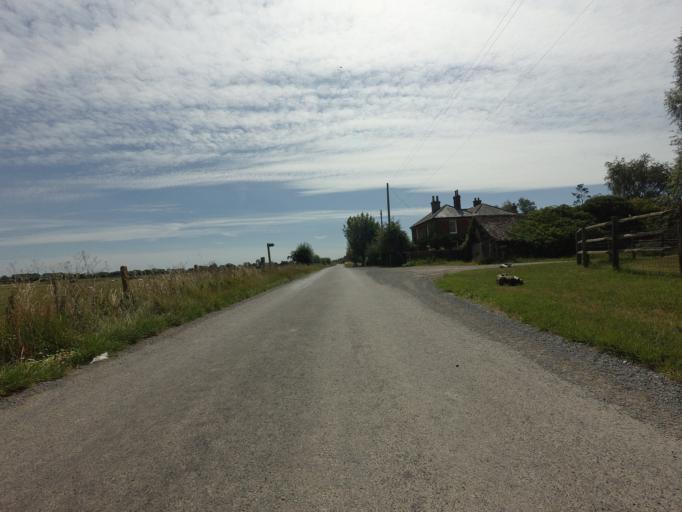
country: GB
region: England
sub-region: Kent
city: Stone
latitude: 51.0055
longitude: 0.7974
